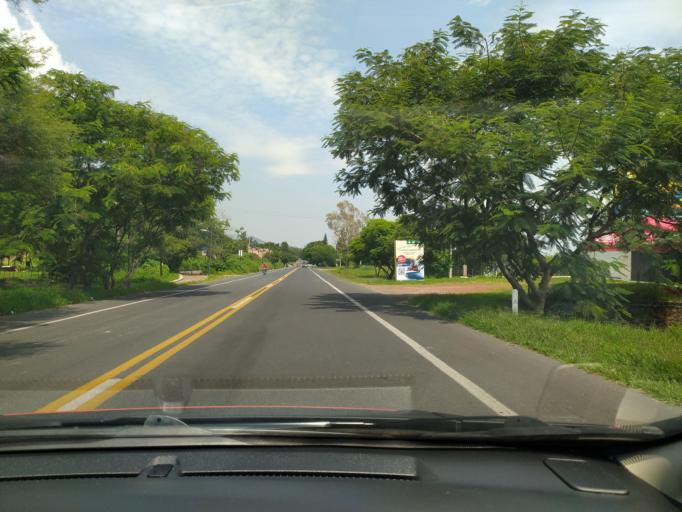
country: MX
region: Jalisco
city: San Juan Cosala
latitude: 20.2940
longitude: -103.3815
